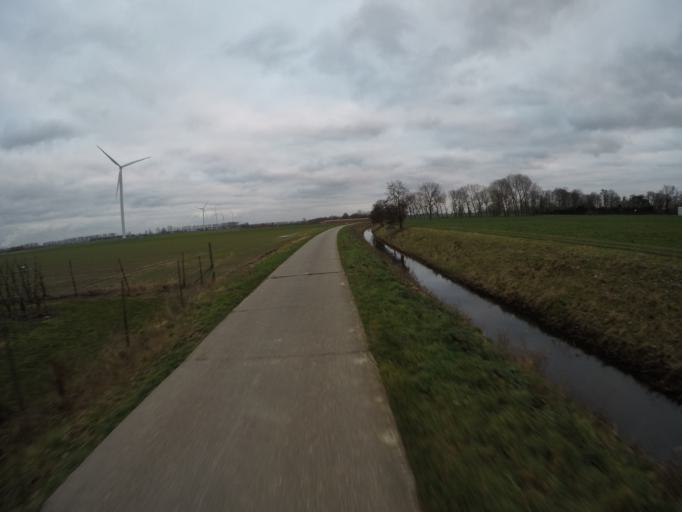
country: BE
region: Flanders
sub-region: Provincie Oost-Vlaanderen
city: Sint-Gillis-Waas
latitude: 51.2301
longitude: 4.1513
